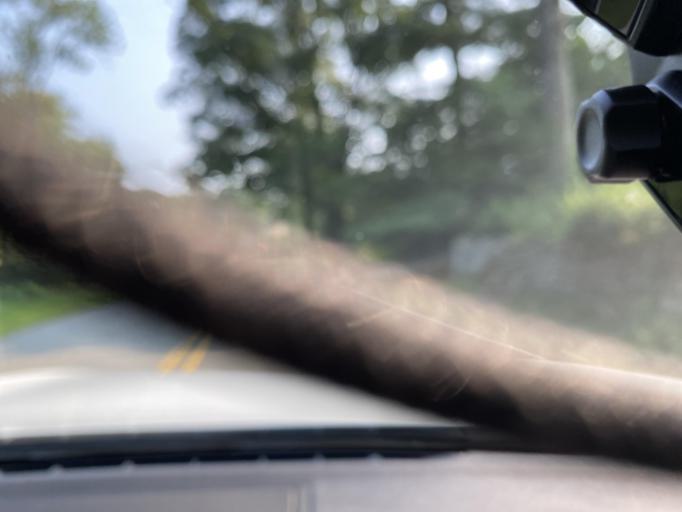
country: US
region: New York
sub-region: Rockland County
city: Airmont
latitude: 41.0922
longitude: -74.1279
